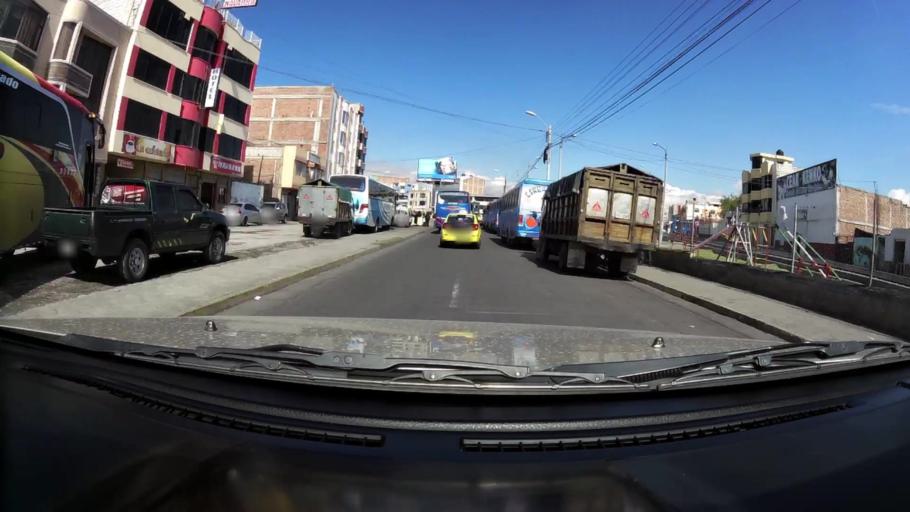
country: EC
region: Chimborazo
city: Riobamba
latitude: -1.6660
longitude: -78.6648
